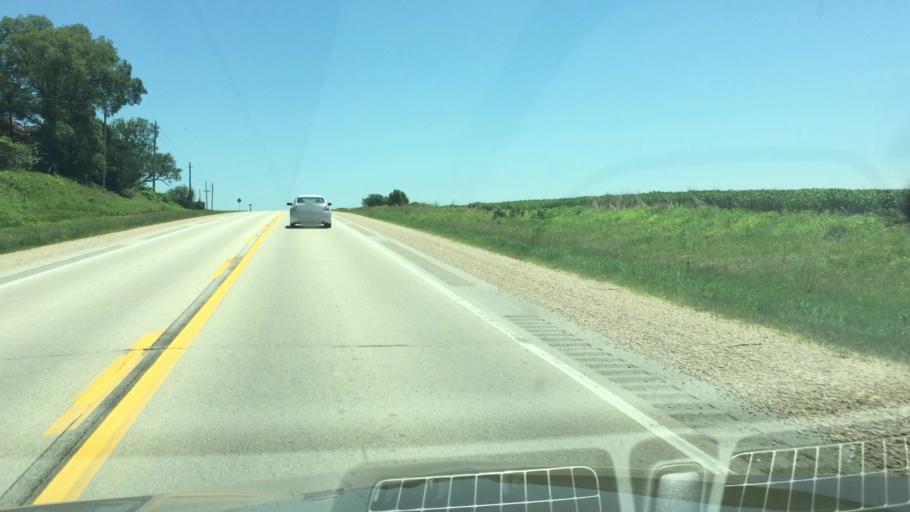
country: US
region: Iowa
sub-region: Jackson County
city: Maquoketa
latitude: 42.0716
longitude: -90.7974
